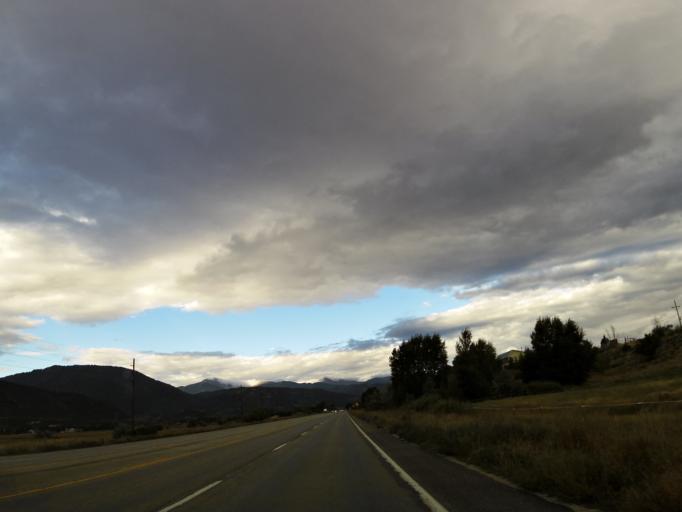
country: US
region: Colorado
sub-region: Chaffee County
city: Salida
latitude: 38.5182
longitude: -106.0530
